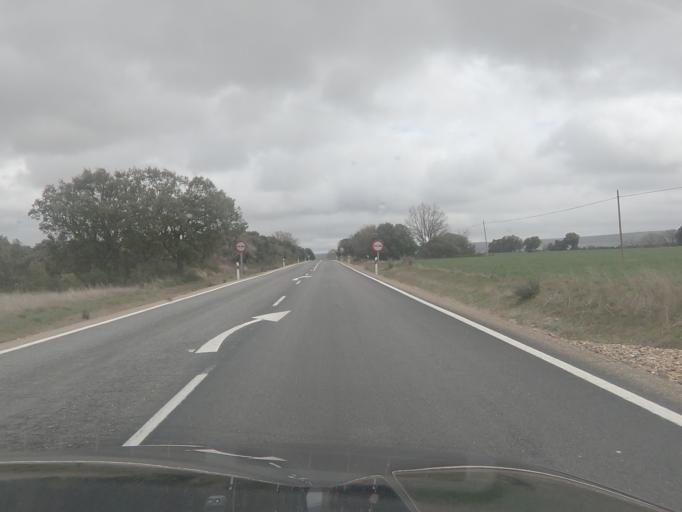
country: ES
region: Castille and Leon
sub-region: Provincia de Zamora
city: Tabara
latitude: 41.8068
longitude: -5.9283
